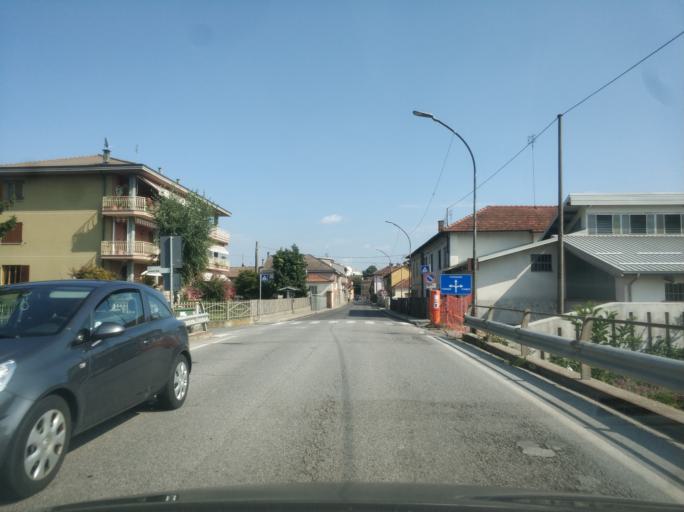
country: IT
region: Piedmont
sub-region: Provincia di Cuneo
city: Centallo
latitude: 44.5023
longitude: 7.5820
